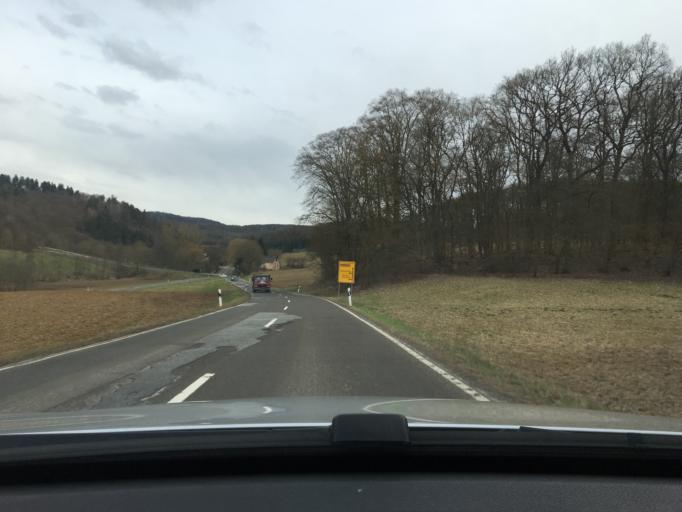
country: DE
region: Rheinland-Pfalz
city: Wurzweiler
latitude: 49.6421
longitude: 7.8626
